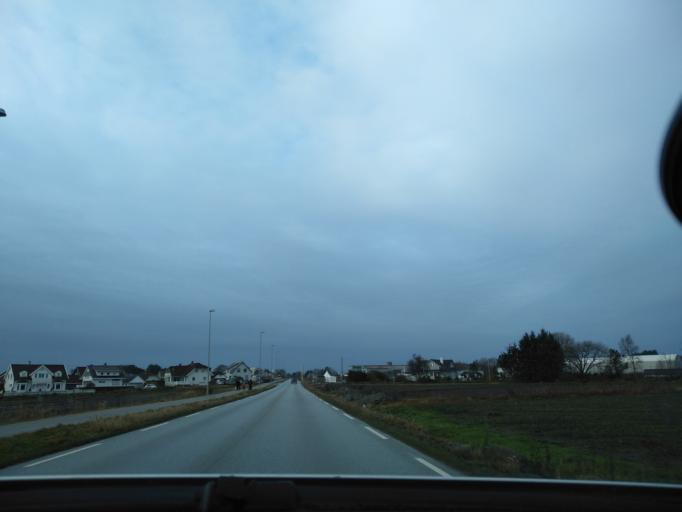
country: NO
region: Rogaland
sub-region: Randaberg
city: Randaberg
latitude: 58.9940
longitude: 5.6413
